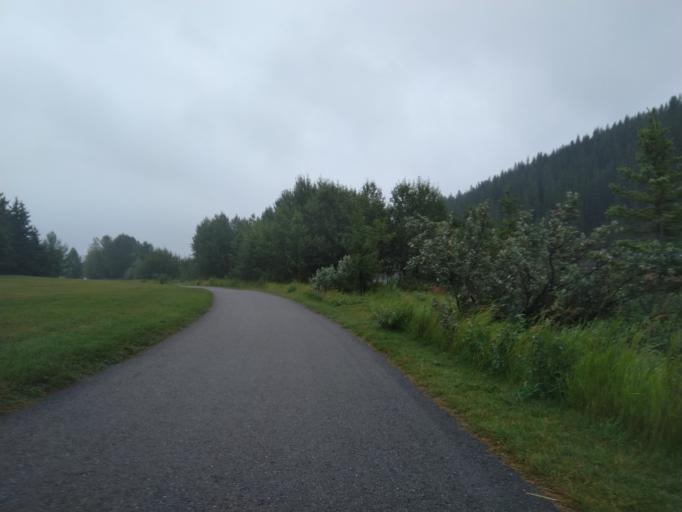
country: CA
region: Alberta
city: Cochrane
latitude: 51.1727
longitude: -114.4753
